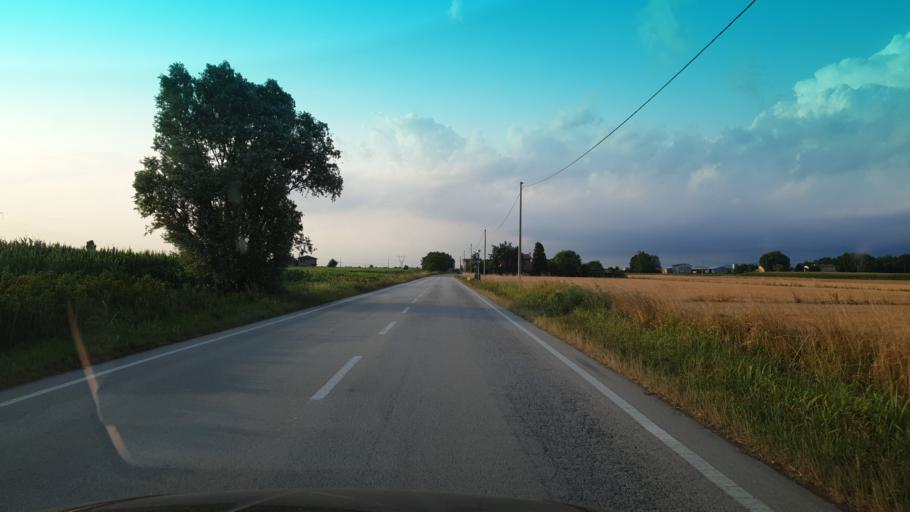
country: IT
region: Veneto
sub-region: Provincia di Rovigo
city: Lendinara
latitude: 45.0605
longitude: 11.5821
